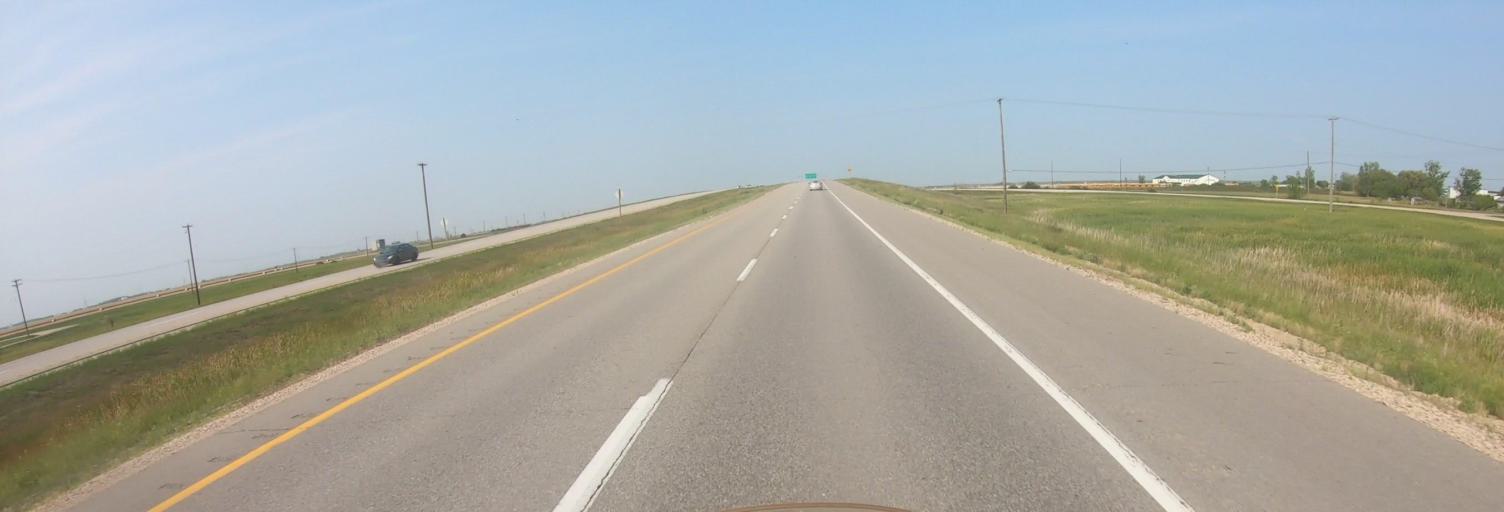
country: CA
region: Manitoba
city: Steinbach
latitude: 49.6776
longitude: -96.6786
